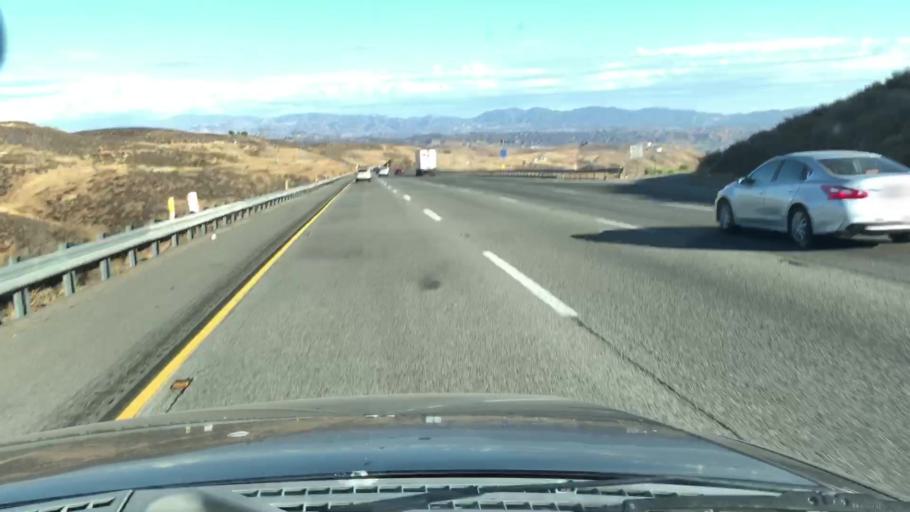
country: US
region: California
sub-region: Los Angeles County
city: Castaic
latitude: 34.5492
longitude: -118.6645
